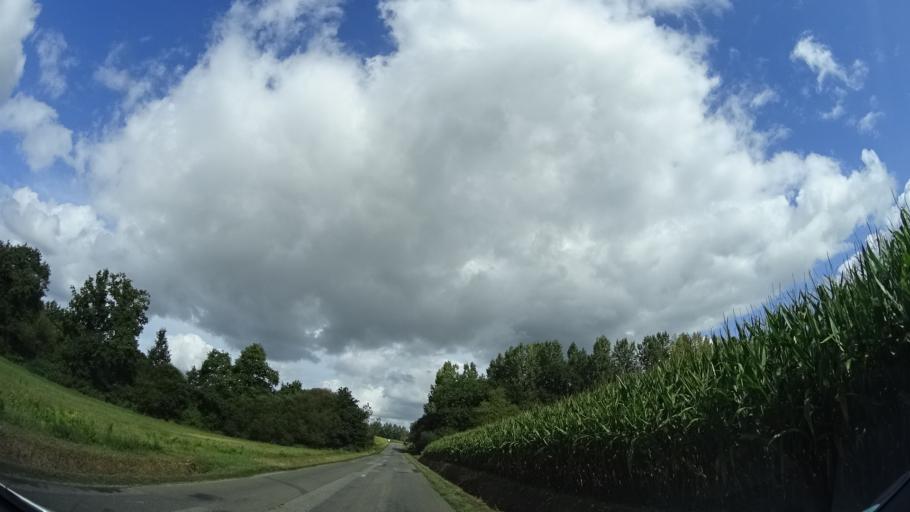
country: FR
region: Brittany
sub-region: Departement d'Ille-et-Vilaine
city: Dinge
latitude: 48.3361
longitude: -1.6907
